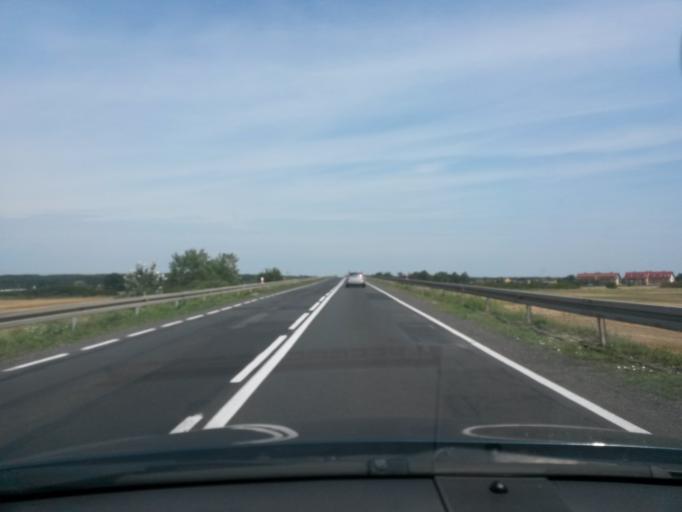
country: PL
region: Lower Silesian Voivodeship
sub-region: Powiat legnicki
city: Prochowice
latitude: 51.2783
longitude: 16.3480
